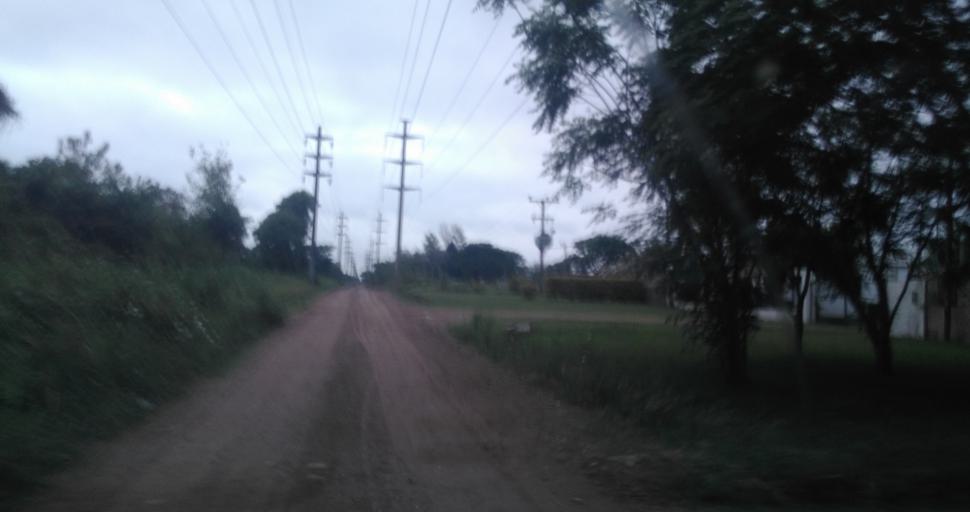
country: AR
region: Chaco
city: Fontana
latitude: -27.4041
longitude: -59.0076
